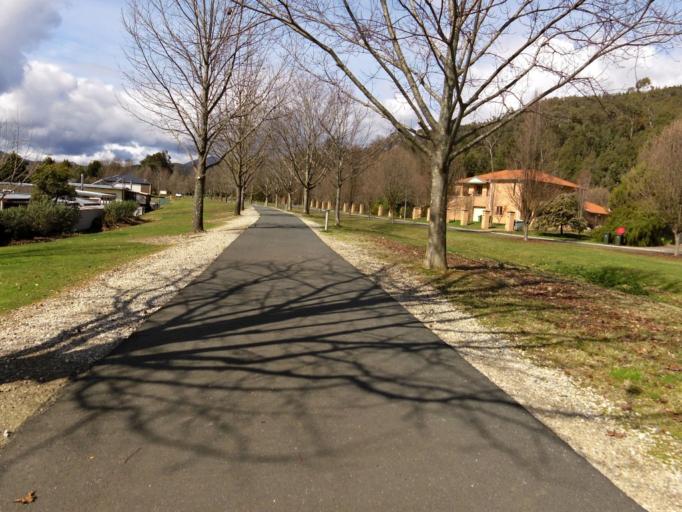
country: AU
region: Victoria
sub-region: Alpine
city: Mount Beauty
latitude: -36.7297
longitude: 146.9514
